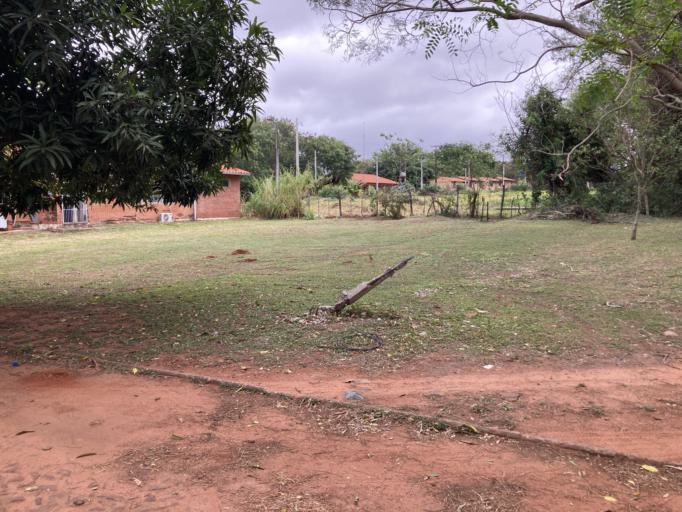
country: PY
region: Central
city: Fernando de la Mora
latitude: -25.3445
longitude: -57.5303
